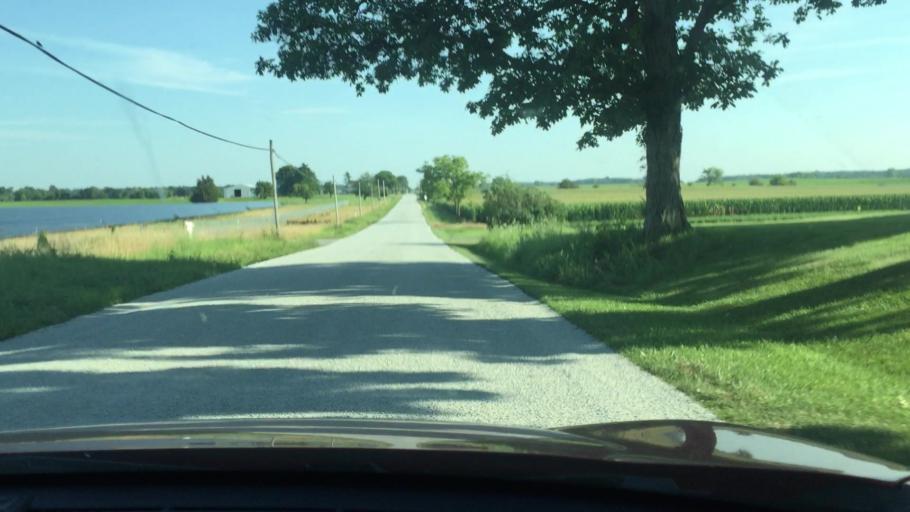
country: US
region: Ohio
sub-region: Hardin County
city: Ada
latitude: 40.7609
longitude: -83.8424
